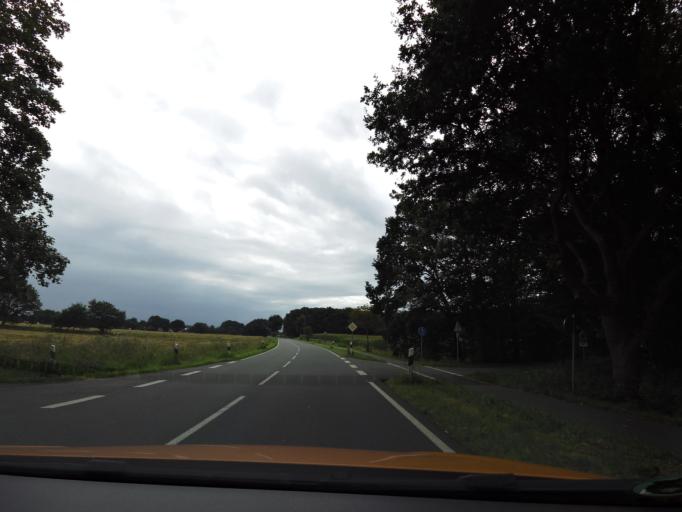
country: DE
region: Lower Saxony
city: Gross Ippener
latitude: 52.9856
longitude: 8.6149
